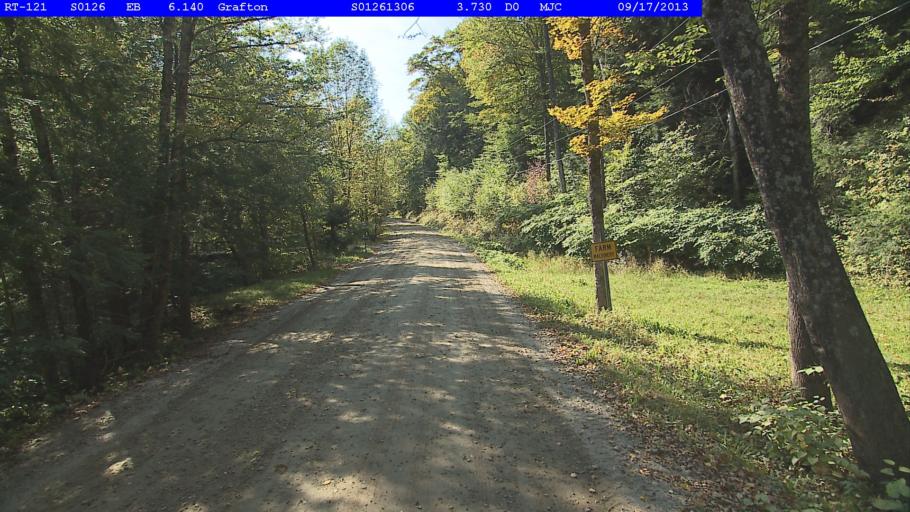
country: US
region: Vermont
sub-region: Windsor County
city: Chester
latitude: 43.1954
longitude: -72.6190
